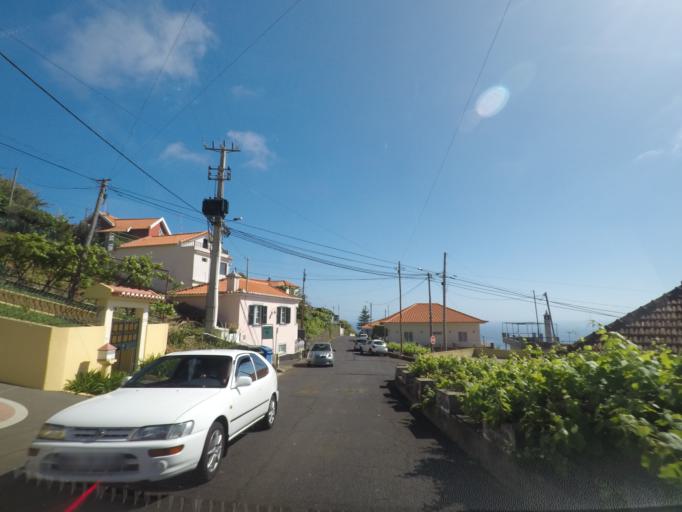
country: PT
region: Madeira
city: Ponta do Sol
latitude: 32.6942
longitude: -17.0964
